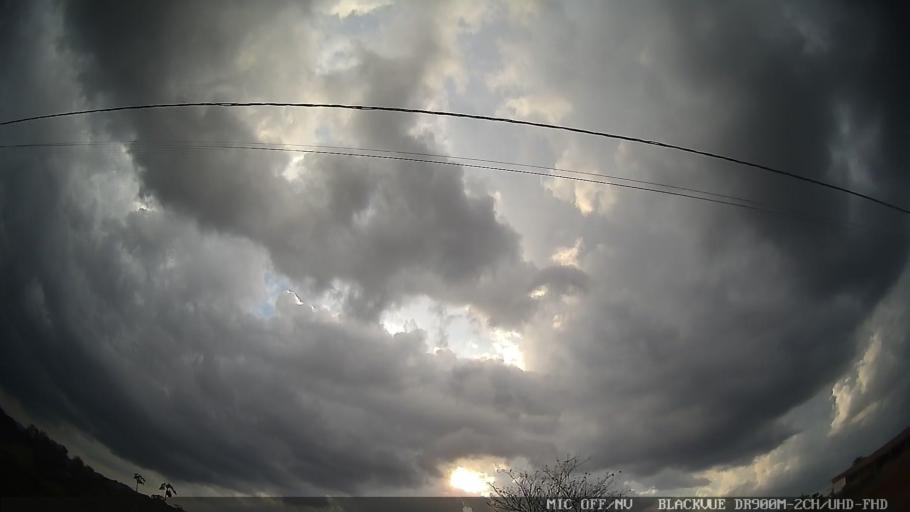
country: BR
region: Sao Paulo
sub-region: Braganca Paulista
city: Braganca Paulista
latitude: -22.9154
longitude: -46.5327
